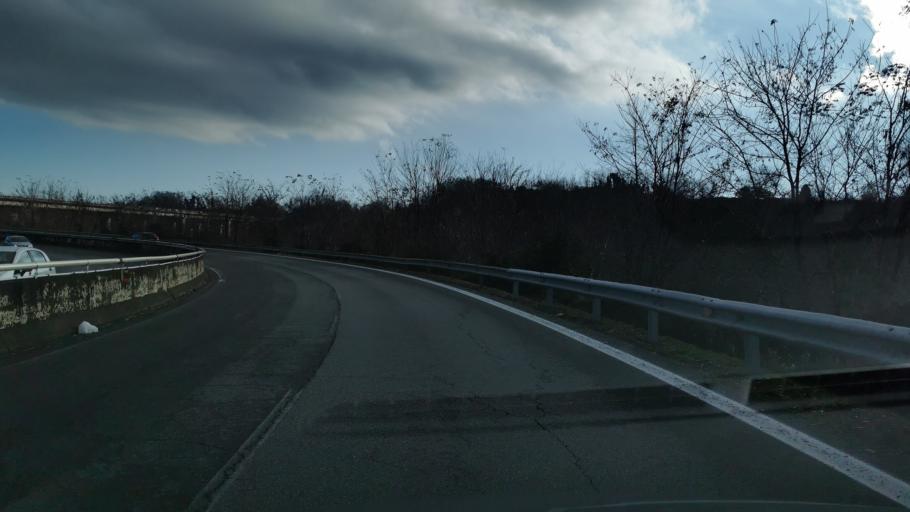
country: IT
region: Piedmont
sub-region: Provincia di Biella
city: Biella
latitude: 45.5624
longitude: 8.0705
